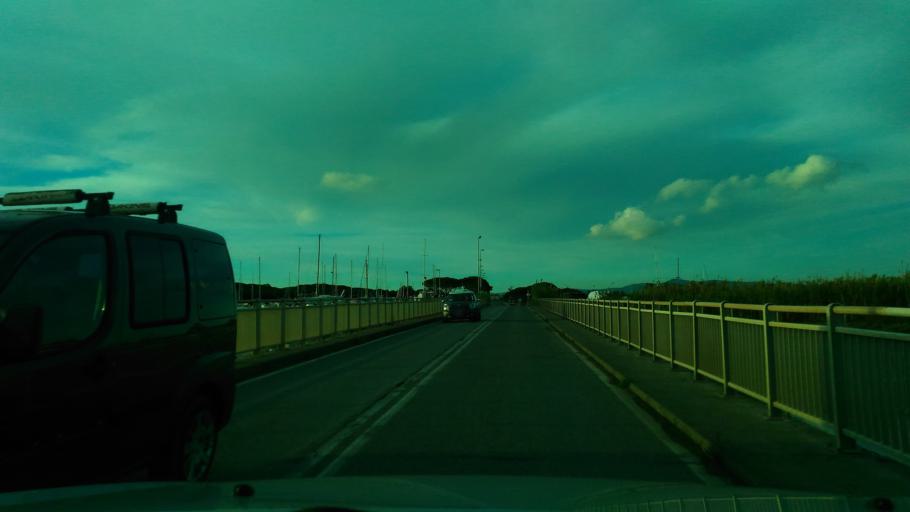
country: IT
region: Tuscany
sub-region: Provincia di Livorno
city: Cecina
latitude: 43.3036
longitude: 10.4935
